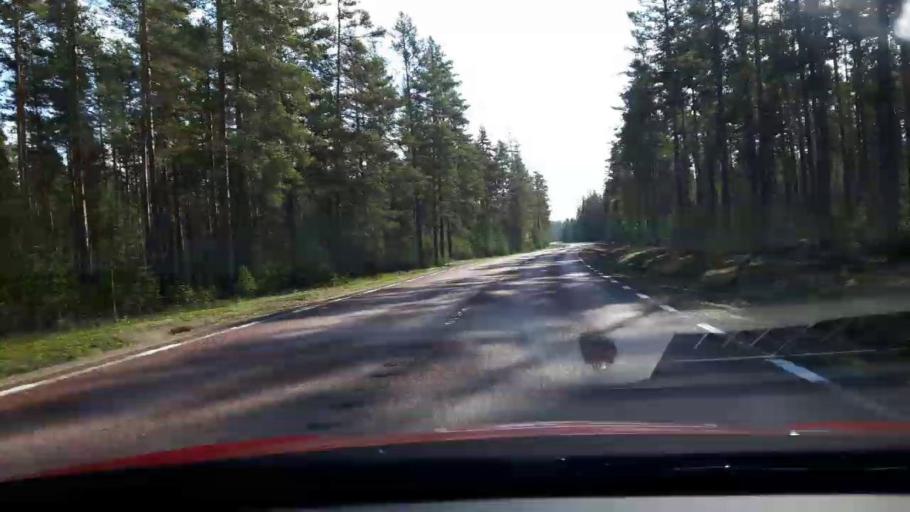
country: SE
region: Gaevleborg
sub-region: Ljusdals Kommun
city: Farila
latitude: 61.9193
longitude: 15.6134
